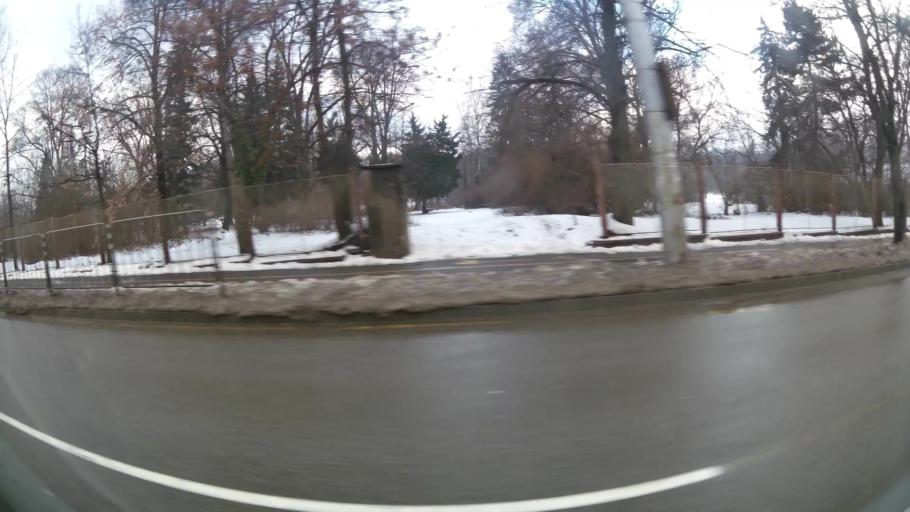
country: BG
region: Sofia-Capital
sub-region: Stolichna Obshtina
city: Sofia
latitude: 42.7155
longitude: 23.2826
